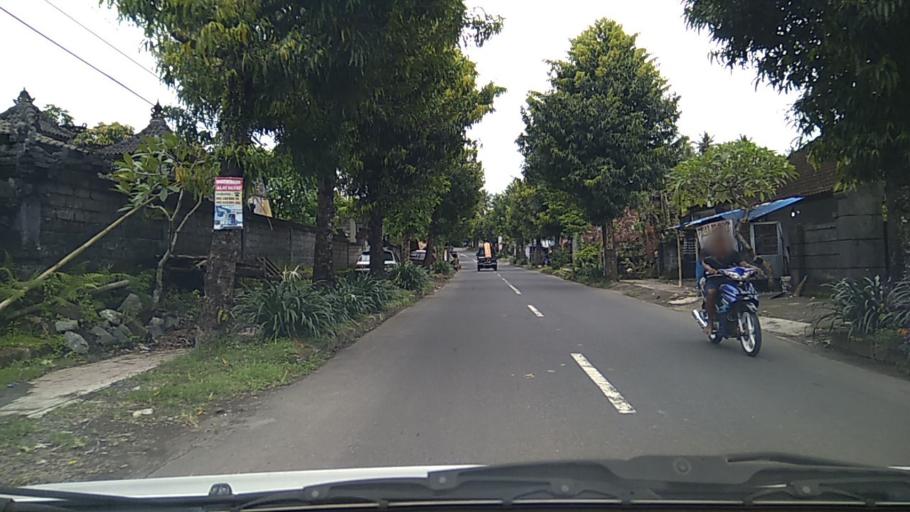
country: ID
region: Bali
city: Banjar Kelodan
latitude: -8.5321
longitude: 115.3485
